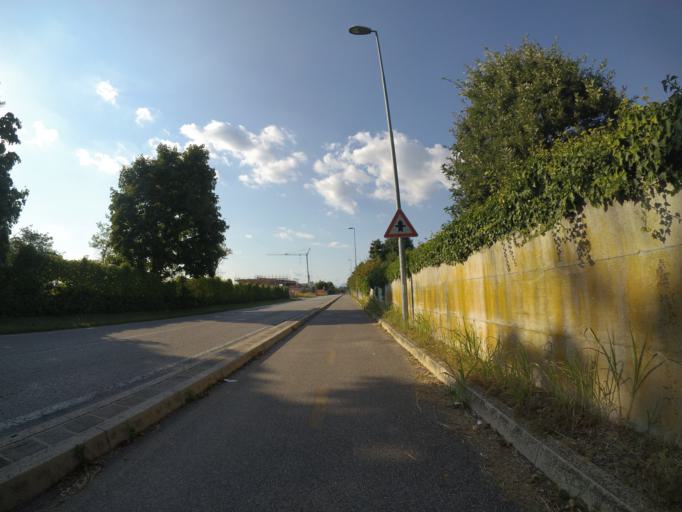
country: IT
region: Friuli Venezia Giulia
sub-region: Provincia di Udine
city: Pasian di Prato
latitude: 46.0378
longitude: 13.2020
